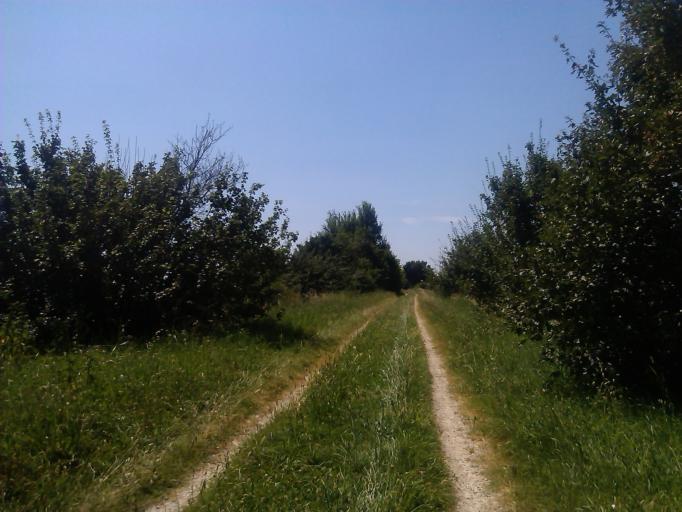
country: IT
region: Tuscany
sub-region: Province of Arezzo
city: Cesa
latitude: 43.3358
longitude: 11.8295
